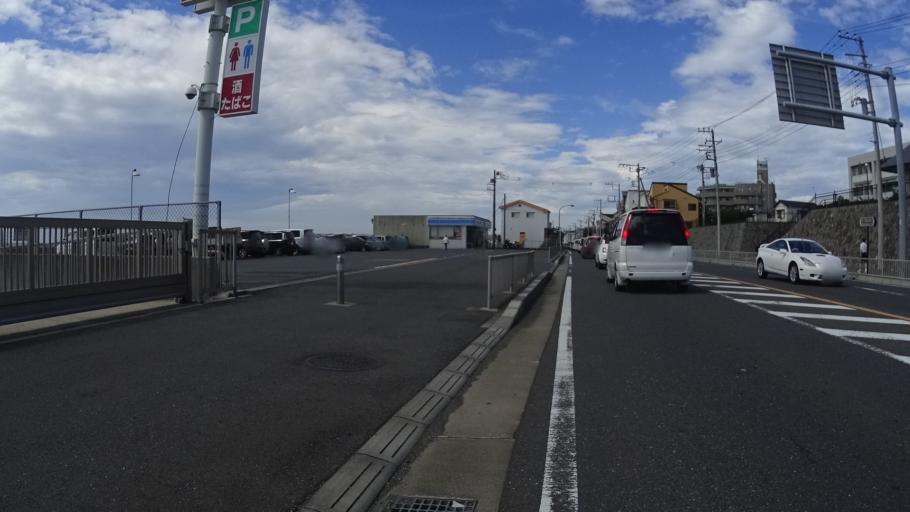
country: JP
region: Kanagawa
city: Yokosuka
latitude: 35.2043
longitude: 139.6801
